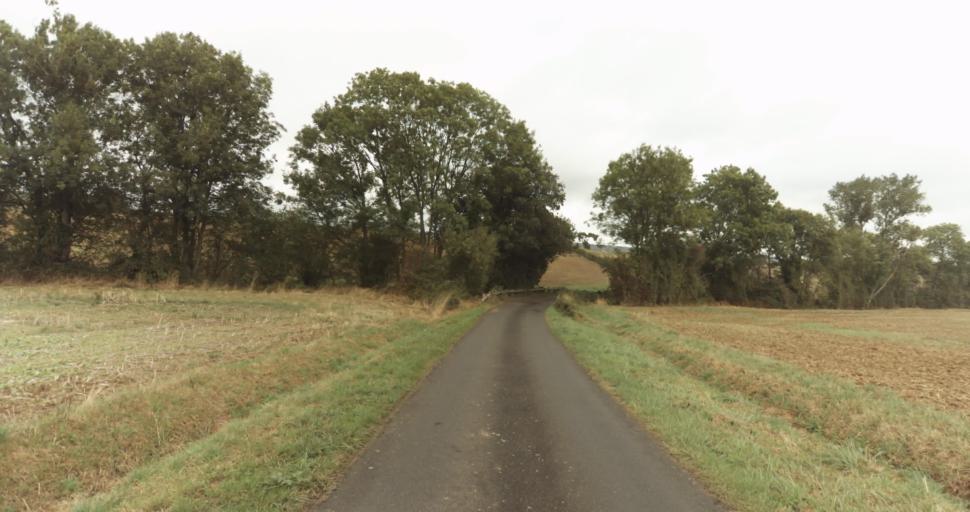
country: FR
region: Lower Normandy
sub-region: Departement de l'Orne
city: Sainte-Gauburge-Sainte-Colombe
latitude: 48.7322
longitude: 0.4475
